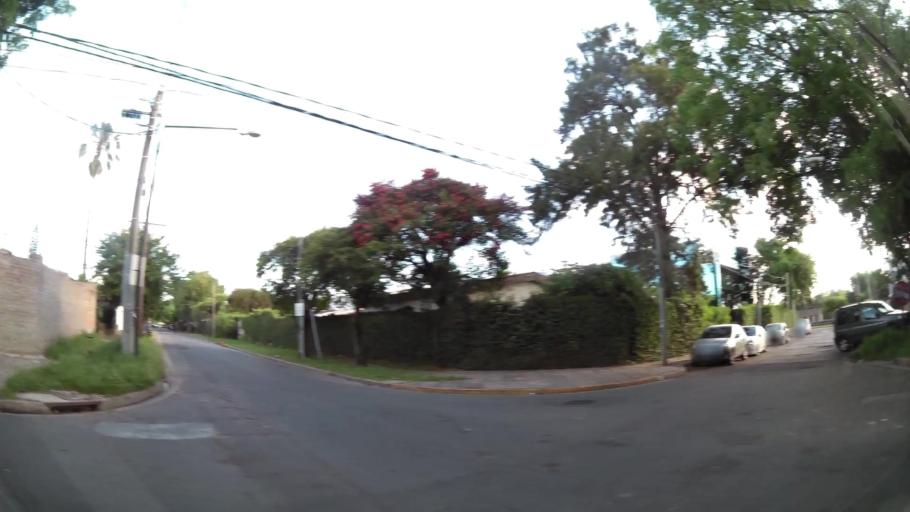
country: AR
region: Buenos Aires
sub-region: Partido de San Isidro
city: San Isidro
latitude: -34.4971
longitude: -58.5501
